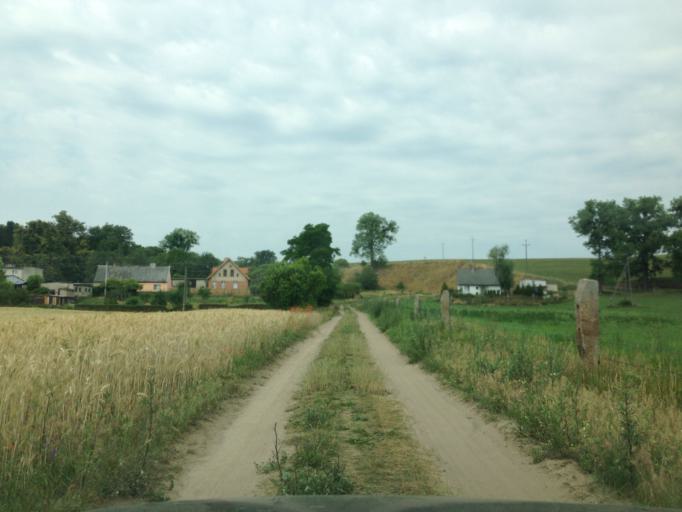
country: PL
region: Kujawsko-Pomorskie
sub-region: Powiat rypinski
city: Wapielsk
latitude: 53.2072
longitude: 19.2641
